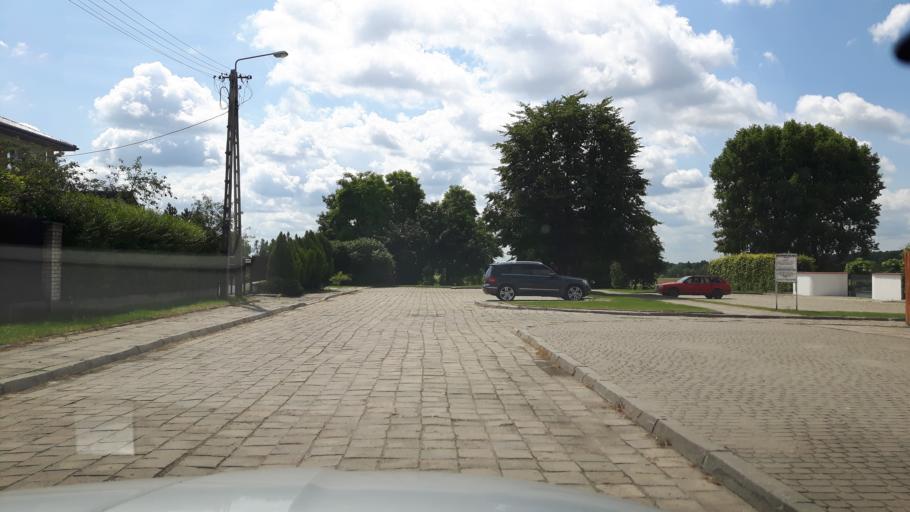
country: PL
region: Masovian Voivodeship
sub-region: Powiat ostrowski
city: Brok
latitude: 52.6979
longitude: 21.8558
